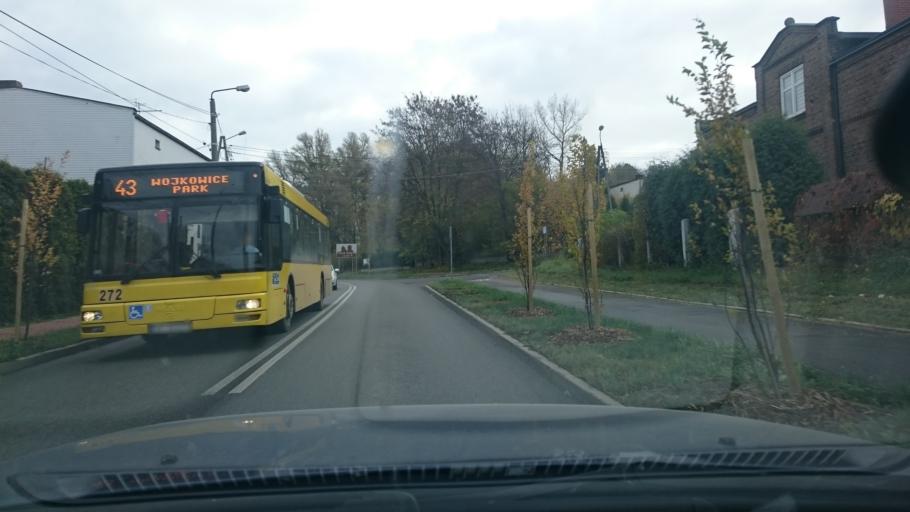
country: PL
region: Silesian Voivodeship
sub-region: Powiat bedzinski
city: Strzyzowice
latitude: 50.3536
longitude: 19.0720
